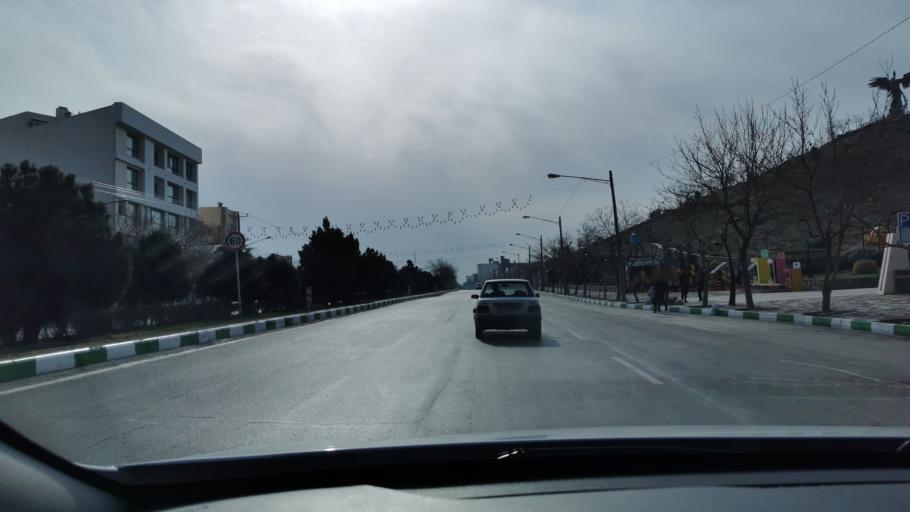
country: IR
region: Razavi Khorasan
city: Mashhad
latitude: 36.2955
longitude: 59.5299
